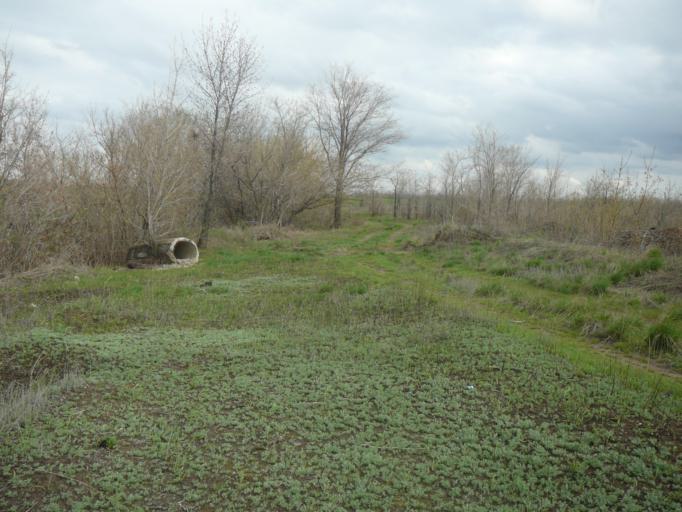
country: RU
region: Saratov
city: Engel's
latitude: 51.4573
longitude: 46.1733
